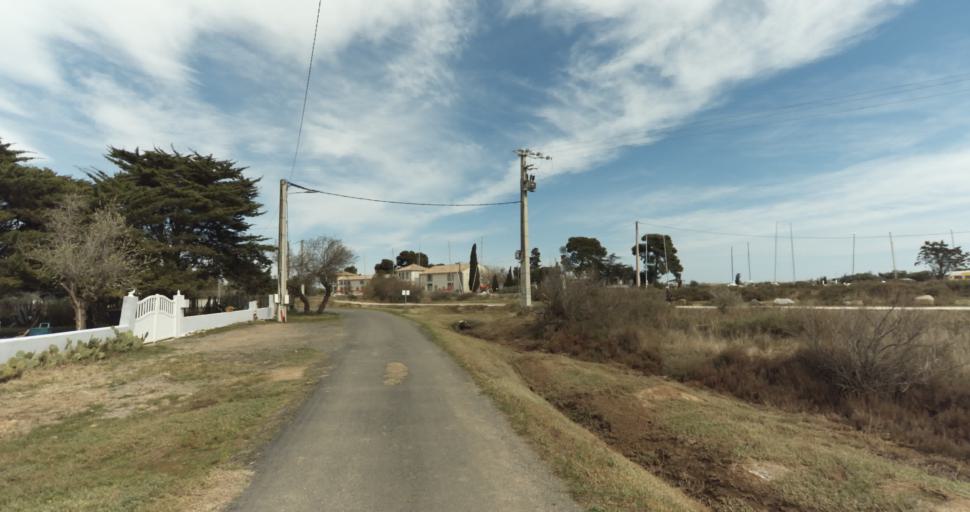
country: FR
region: Languedoc-Roussillon
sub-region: Departement de l'Herault
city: Marseillan
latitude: 43.3361
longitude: 3.5363
